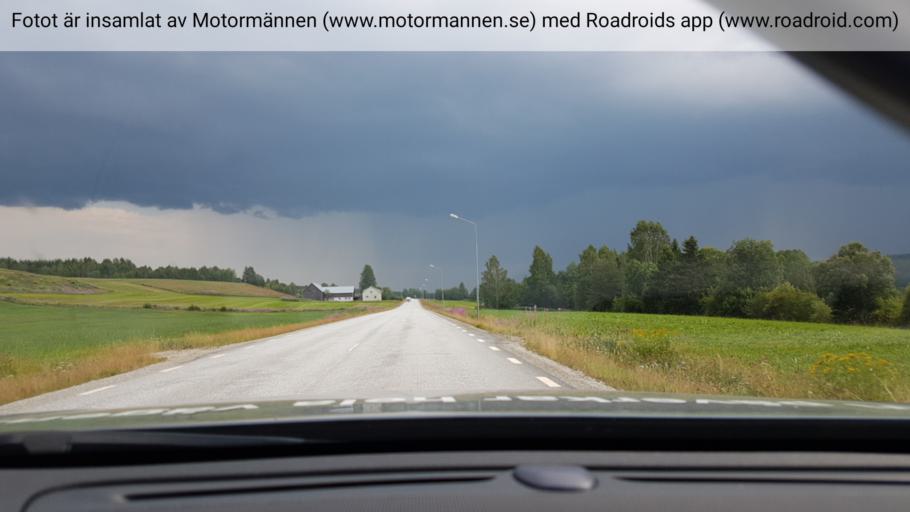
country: SE
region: Vaesterbotten
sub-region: Vindelns Kommun
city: Vindeln
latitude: 64.1729
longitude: 19.4863
